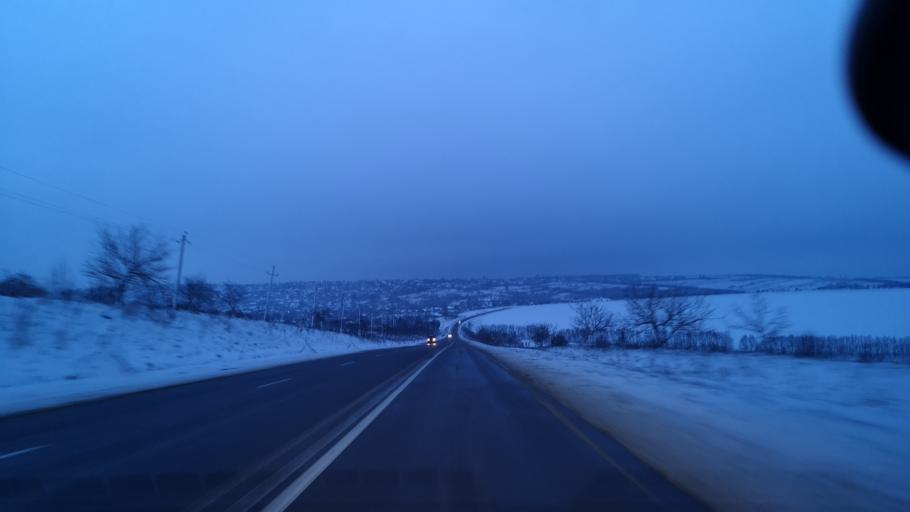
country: MD
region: Soldanesti
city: Soldanesti
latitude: 47.7135
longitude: 28.8474
